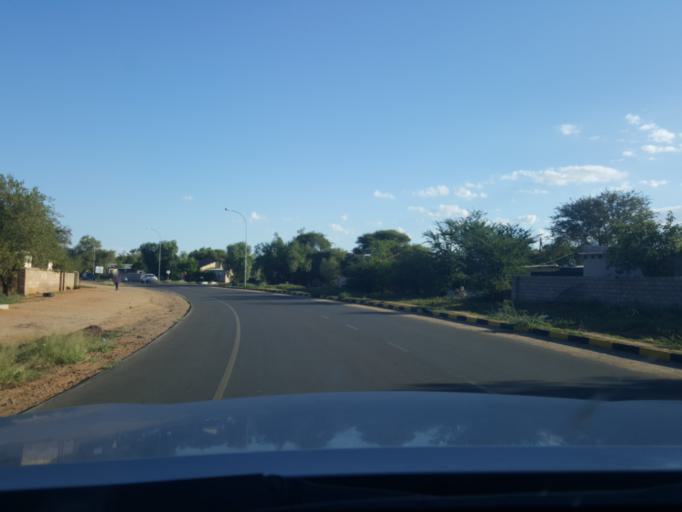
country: BW
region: South East
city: Gaborone
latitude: -24.6210
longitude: 25.9438
